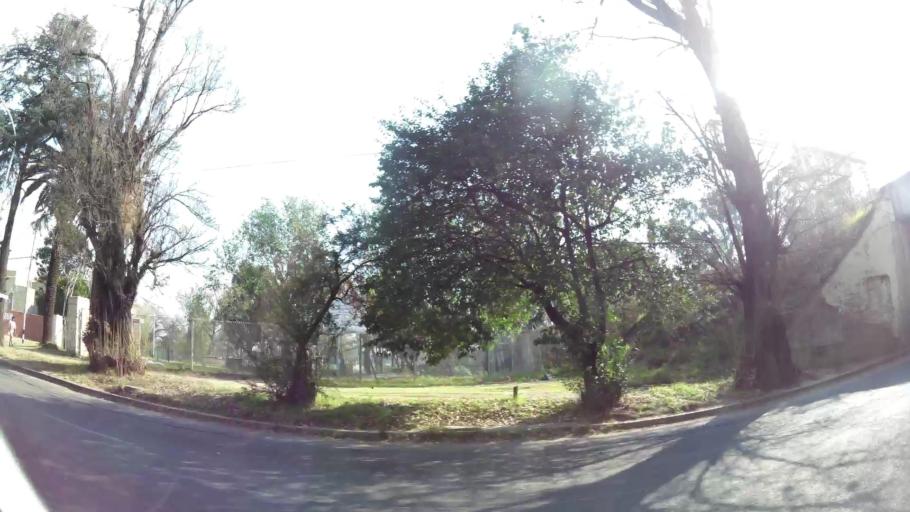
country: ZA
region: Gauteng
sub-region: Ekurhuleni Metropolitan Municipality
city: Boksburg
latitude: -26.2192
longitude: 28.2533
